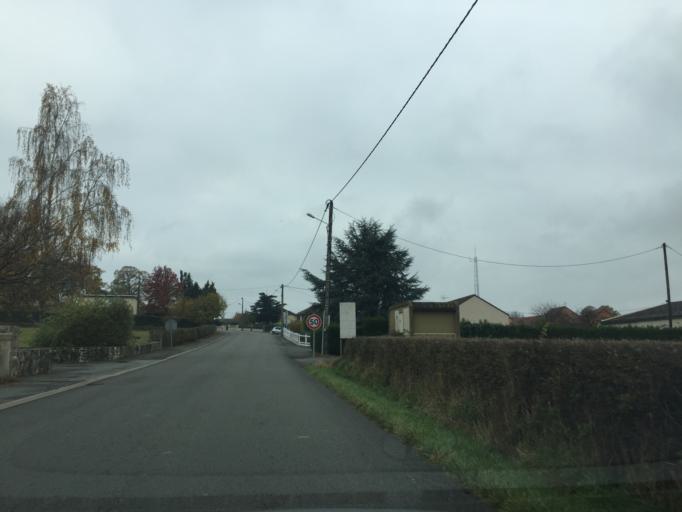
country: FR
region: Limousin
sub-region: Departement de la Creuse
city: Gouzon
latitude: 46.1174
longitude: 2.1793
